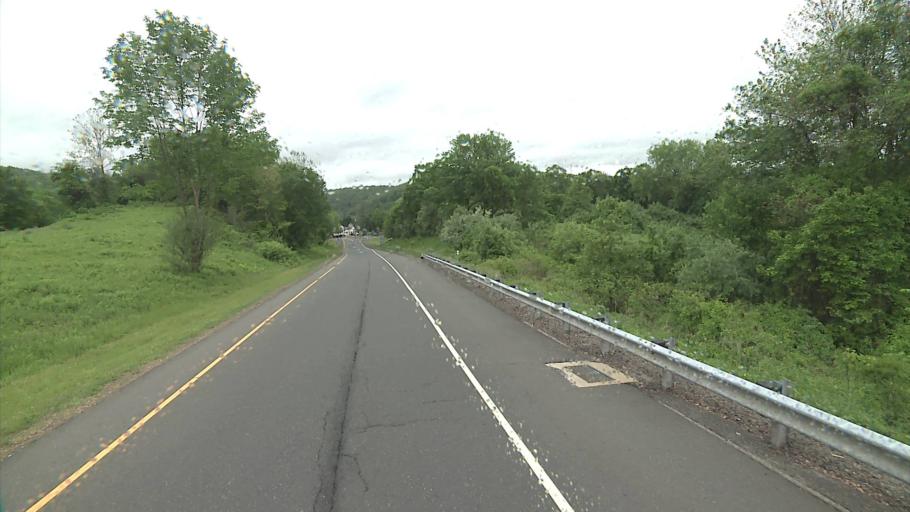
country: US
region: Connecticut
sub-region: New Haven County
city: Heritage Village
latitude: 41.4605
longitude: -73.2327
